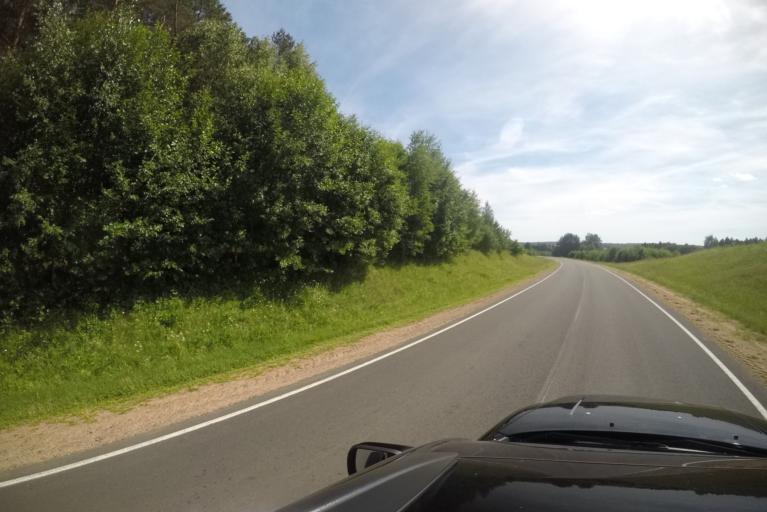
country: BY
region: Grodnenskaya
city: Hal'shany
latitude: 54.2735
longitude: 26.0337
